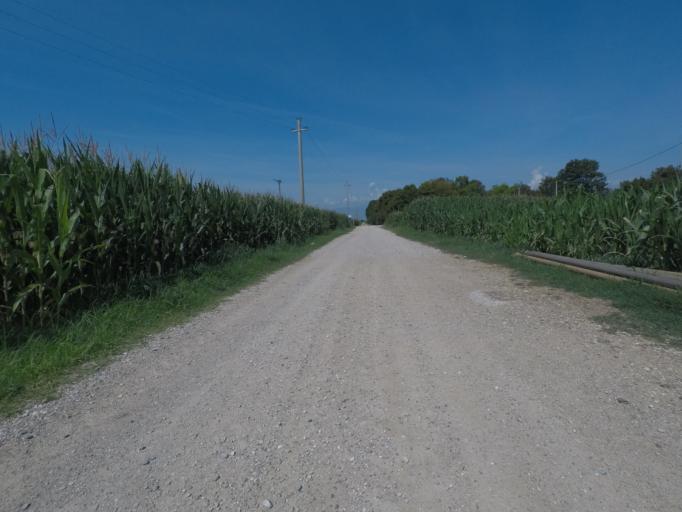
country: IT
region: Friuli Venezia Giulia
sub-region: Provincia di Udine
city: Flaibano
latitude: 46.0814
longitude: 12.9842
